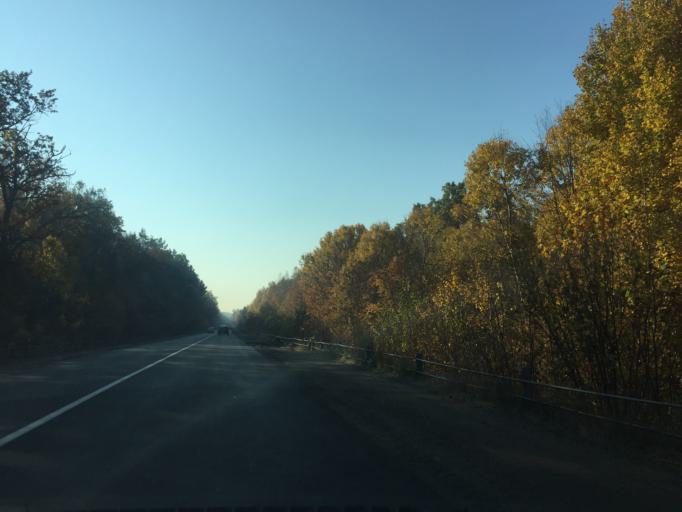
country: BY
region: Gomel
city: Gomel
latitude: 52.4134
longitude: 30.8287
